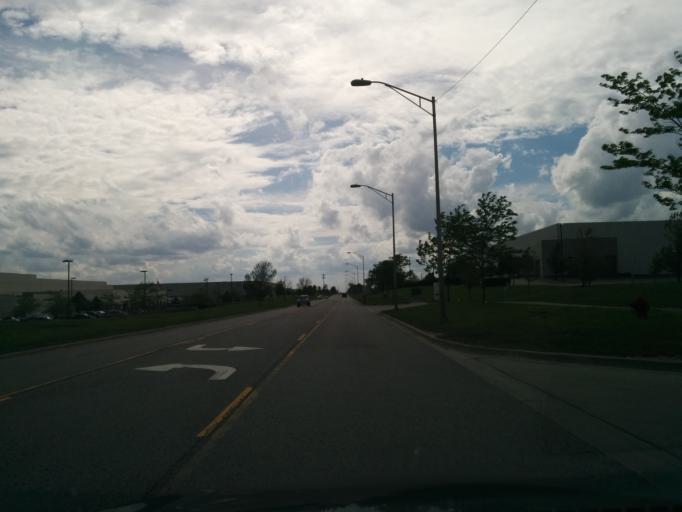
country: US
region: Illinois
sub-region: Will County
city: Romeoville
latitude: 41.6246
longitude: -88.1075
